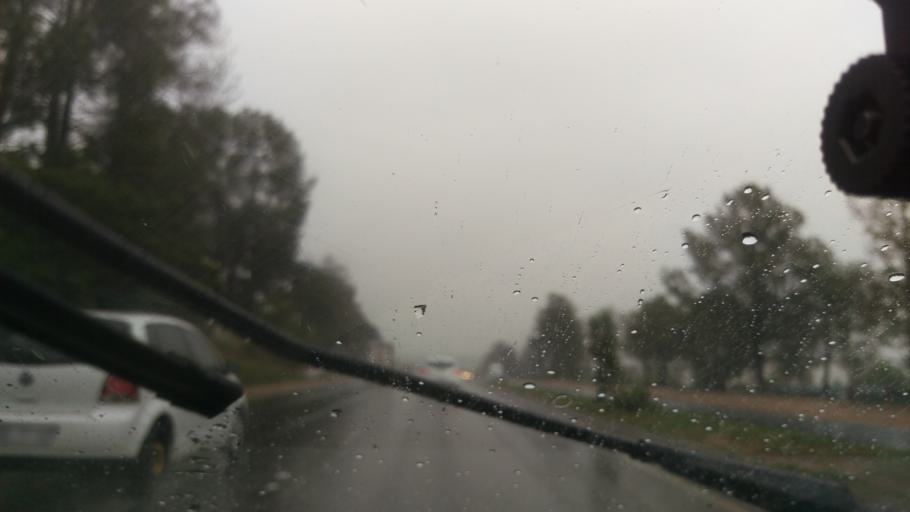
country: ZA
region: Gauteng
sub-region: City of Johannesburg Metropolitan Municipality
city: Diepsloot
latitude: -26.0261
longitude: 27.9878
